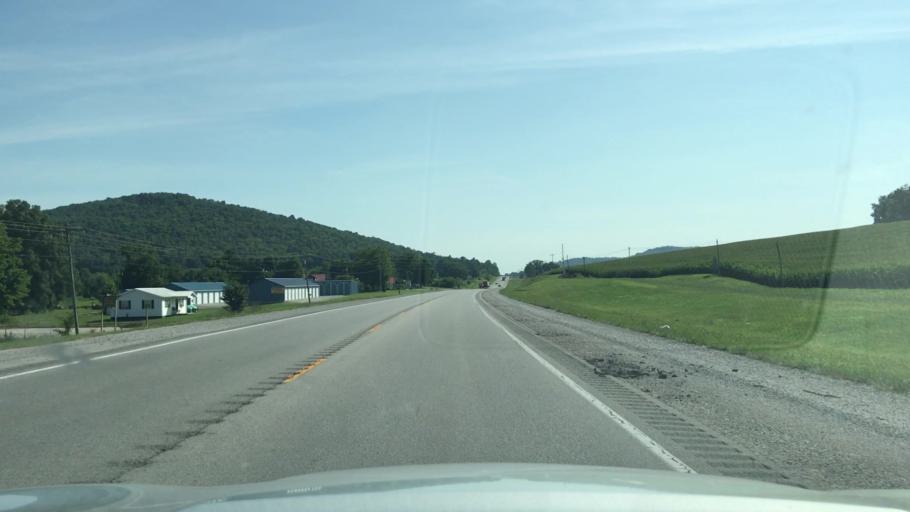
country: US
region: Kentucky
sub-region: Wayne County
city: Monticello
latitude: 36.7882
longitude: -84.9433
